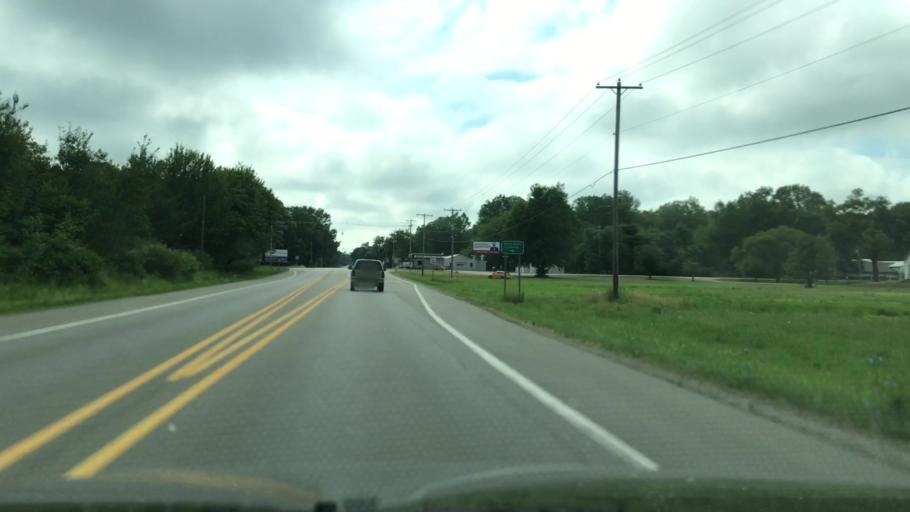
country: US
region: Michigan
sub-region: Ottawa County
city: Spring Lake
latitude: 43.0739
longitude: -86.1437
